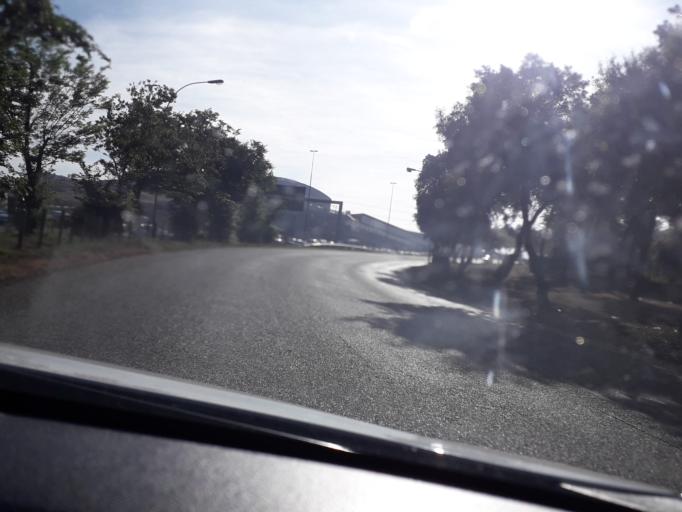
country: ZA
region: Gauteng
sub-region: Ekurhuleni Metropolitan Municipality
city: Germiston
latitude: -26.1647
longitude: 28.1740
